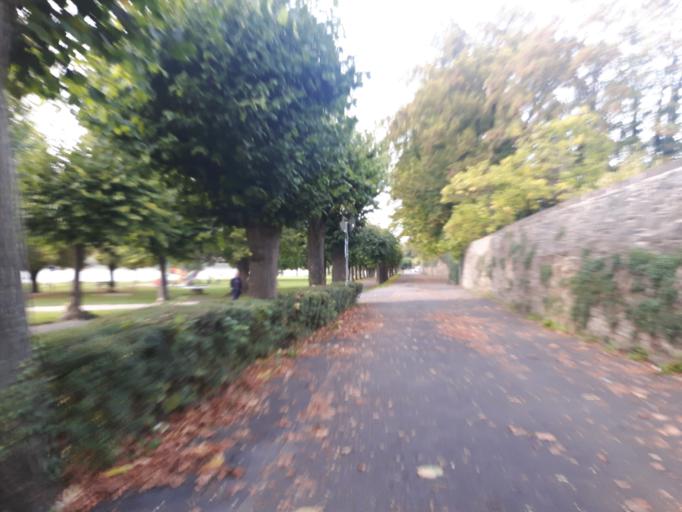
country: DE
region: Rheinland-Pfalz
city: Bad Honningen
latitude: 50.5164
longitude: 7.3040
